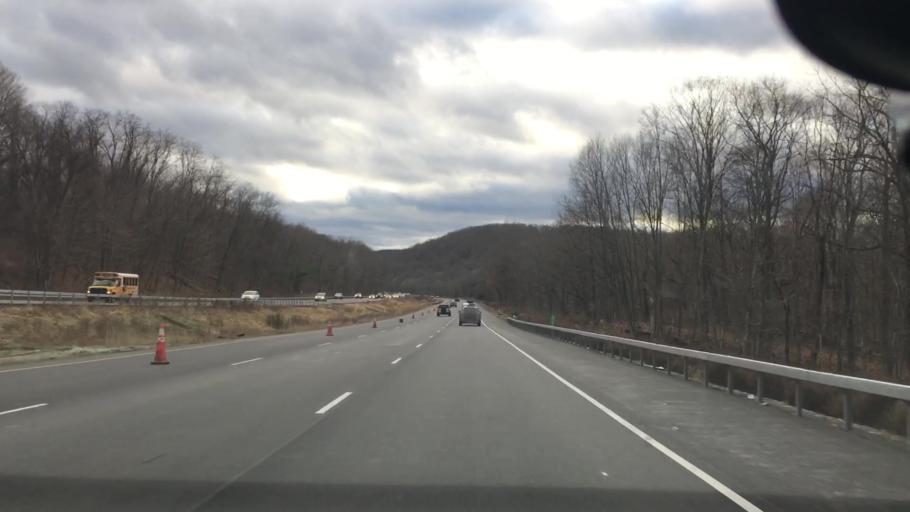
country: US
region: New York
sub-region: Putnam County
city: Brewster
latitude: 41.3722
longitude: -73.6153
